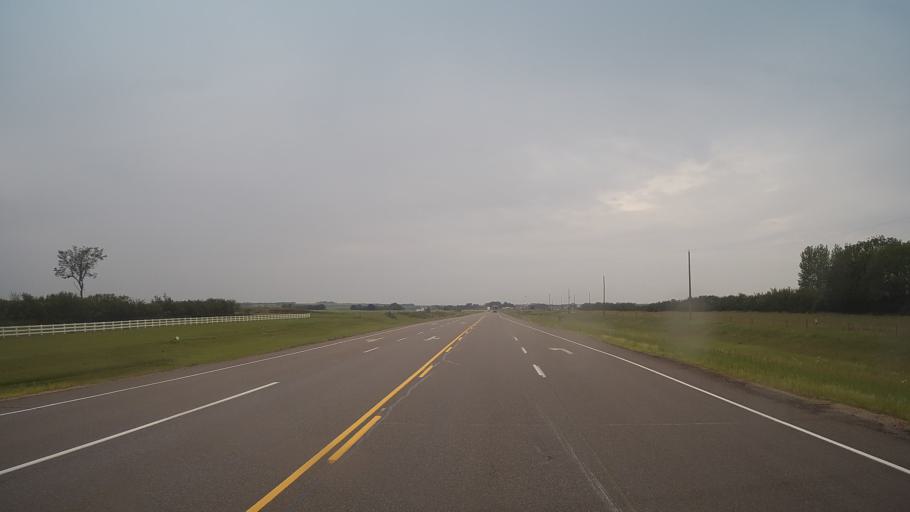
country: CA
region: Saskatchewan
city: Dalmeny
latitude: 52.1292
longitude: -106.8846
